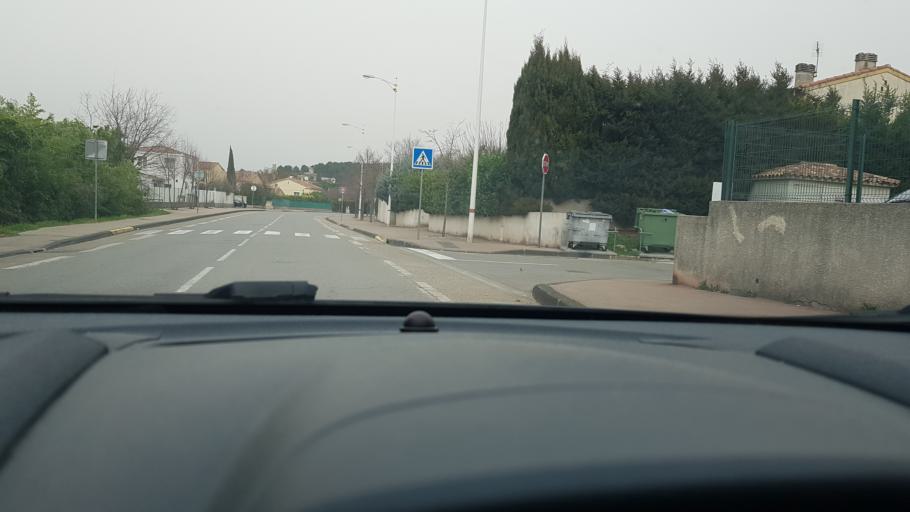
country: FR
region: Provence-Alpes-Cote d'Azur
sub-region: Departement des Bouches-du-Rhone
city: Gardanne
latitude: 43.4495
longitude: 5.4729
